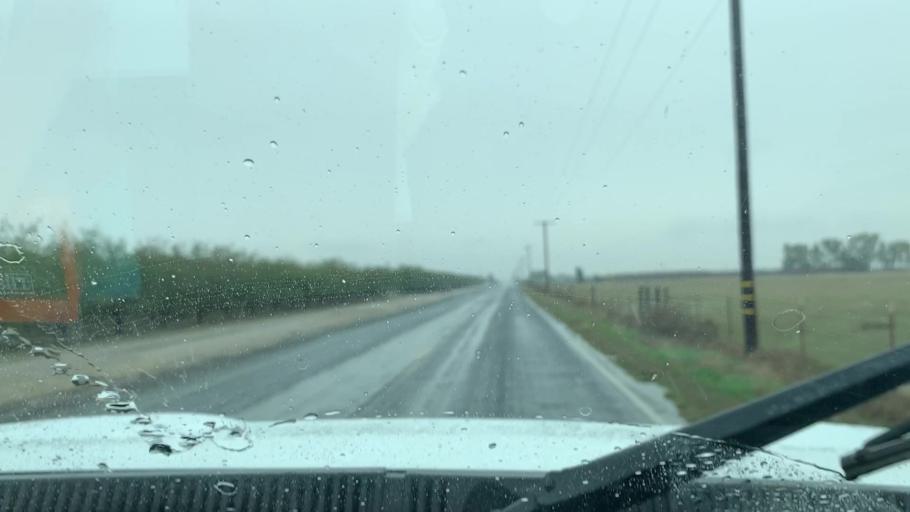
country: US
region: California
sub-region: Tulare County
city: Earlimart
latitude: 35.8919
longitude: -119.3343
